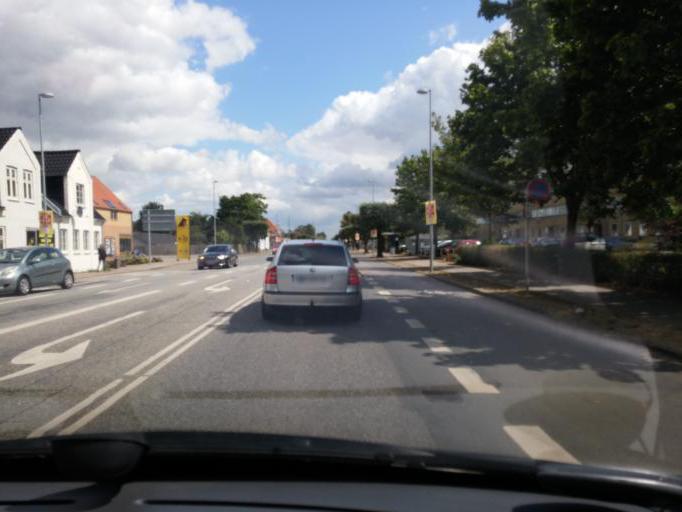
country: DK
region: South Denmark
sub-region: Odense Kommune
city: Odense
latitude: 55.3930
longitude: 10.4222
